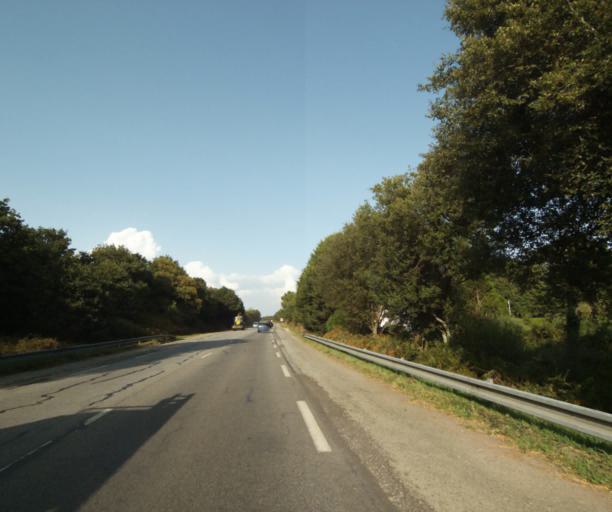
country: FR
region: Brittany
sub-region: Departement du Morbihan
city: Riantec
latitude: 47.7474
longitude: -3.2963
